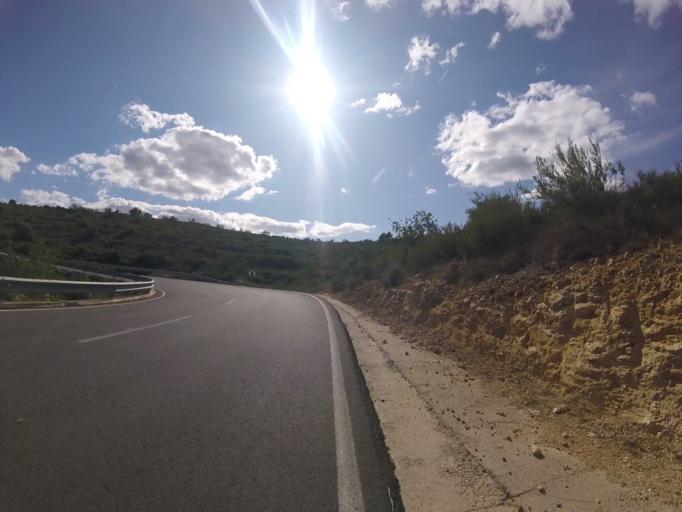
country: ES
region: Valencia
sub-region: Provincia de Castello
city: Cuevas de Vinroma
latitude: 40.3151
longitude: 0.1341
